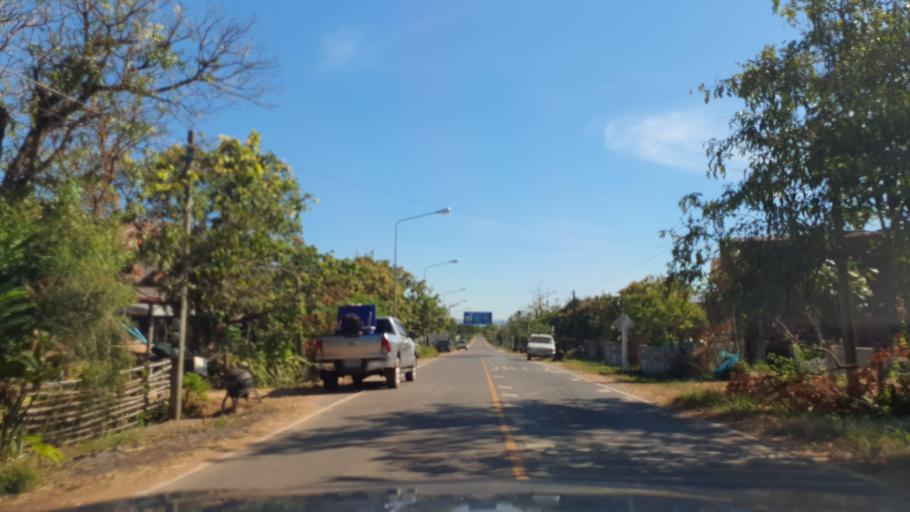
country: TH
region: Kalasin
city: Khao Wong
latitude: 16.7325
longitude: 104.0967
